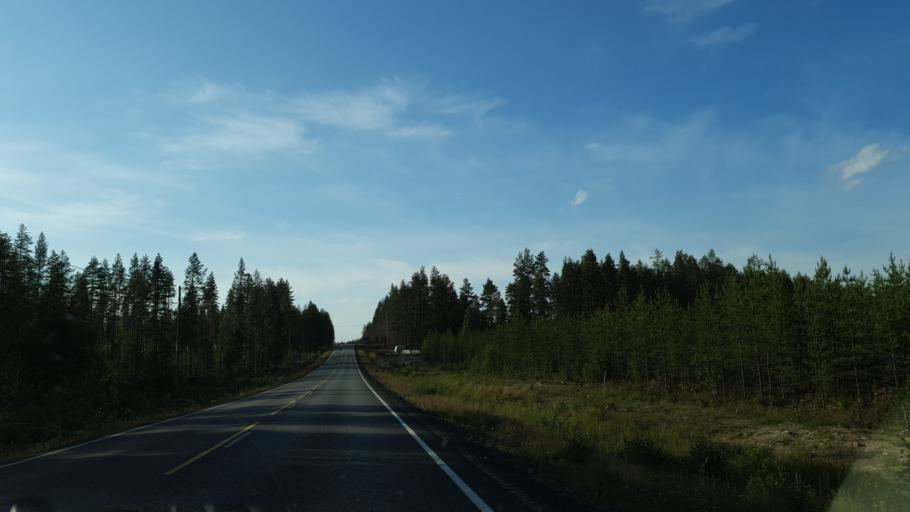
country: FI
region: Kainuu
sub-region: Kehys-Kainuu
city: Kuhmo
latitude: 64.0937
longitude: 29.4789
